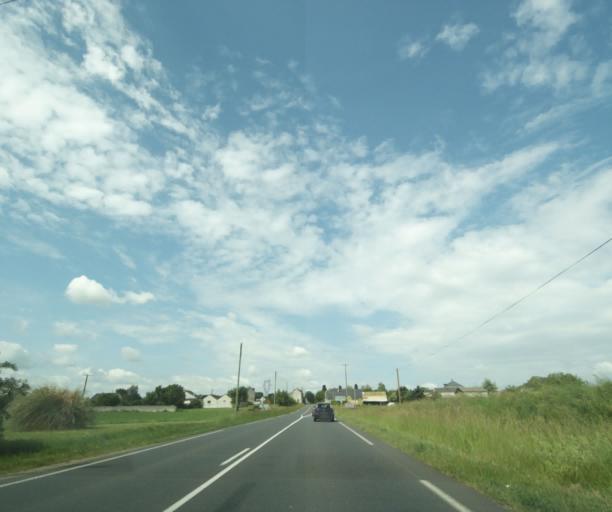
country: FR
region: Pays de la Loire
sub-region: Departement de Maine-et-Loire
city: Distre
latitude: 47.1931
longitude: -0.1268
